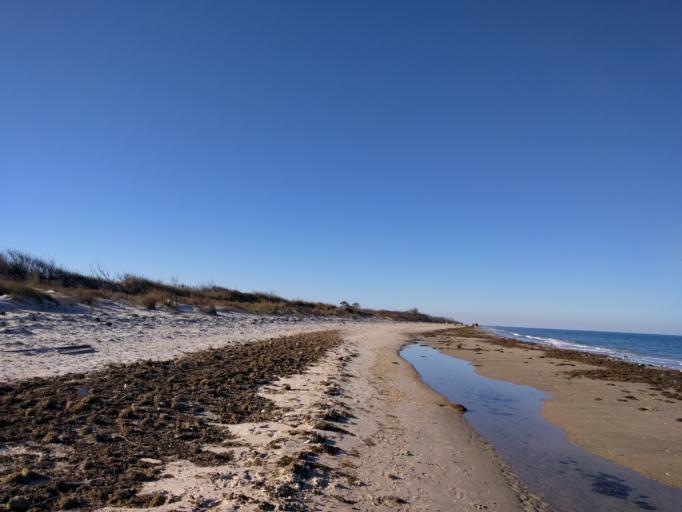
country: US
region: Virginia
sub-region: City of Poquoson
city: Poquoson
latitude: 37.0925
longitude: -76.2732
